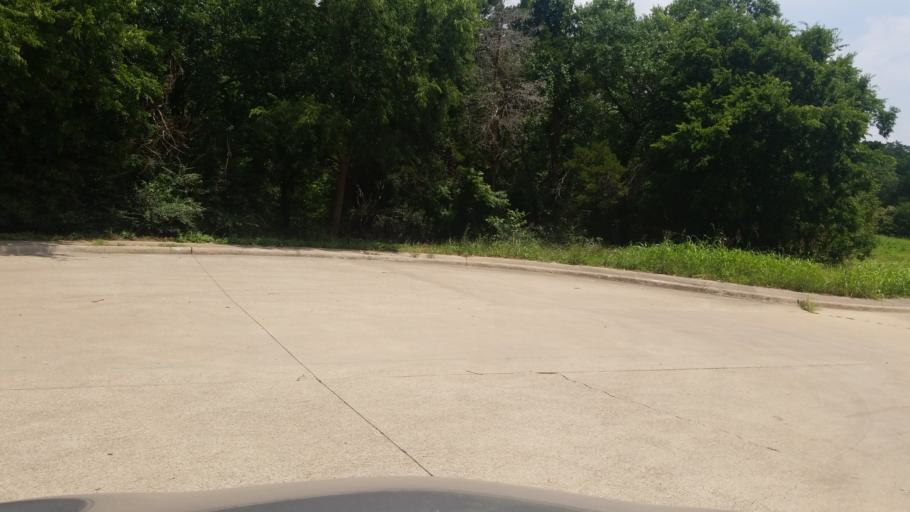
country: US
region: Texas
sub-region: Dallas County
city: Duncanville
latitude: 32.6838
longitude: -96.9234
